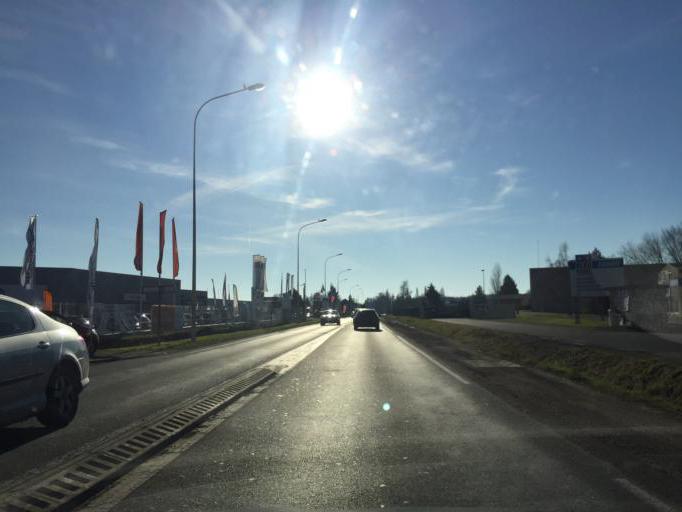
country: FR
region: Auvergne
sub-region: Departement de l'Allier
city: Saint-Remy-en-Rollat
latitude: 46.1560
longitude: 3.3933
